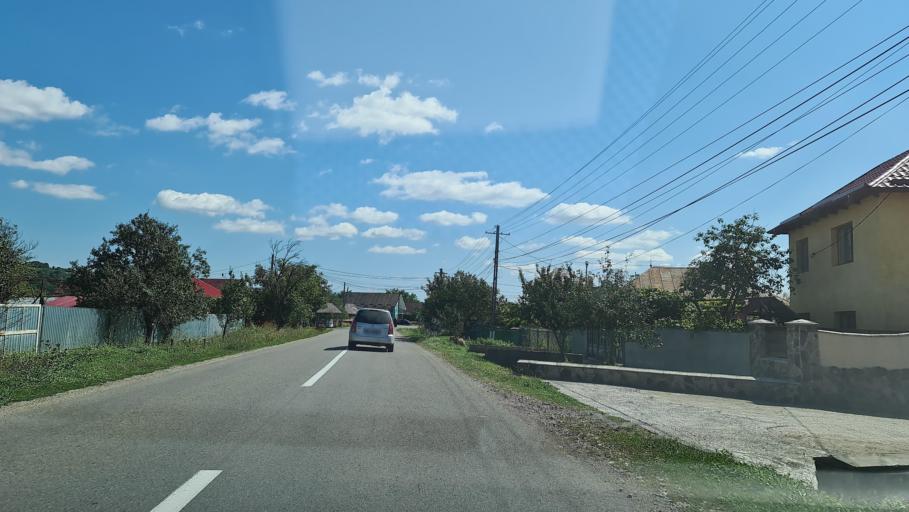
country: RO
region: Bacau
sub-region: Comuna Balcani
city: Ludasi
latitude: 46.6104
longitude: 26.5969
